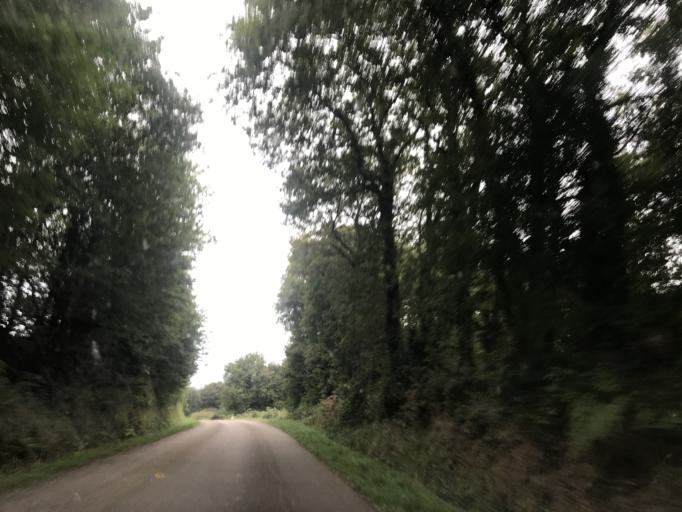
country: FR
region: Brittany
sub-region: Departement du Finistere
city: Plouneour-Menez
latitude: 48.3886
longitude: -3.9005
